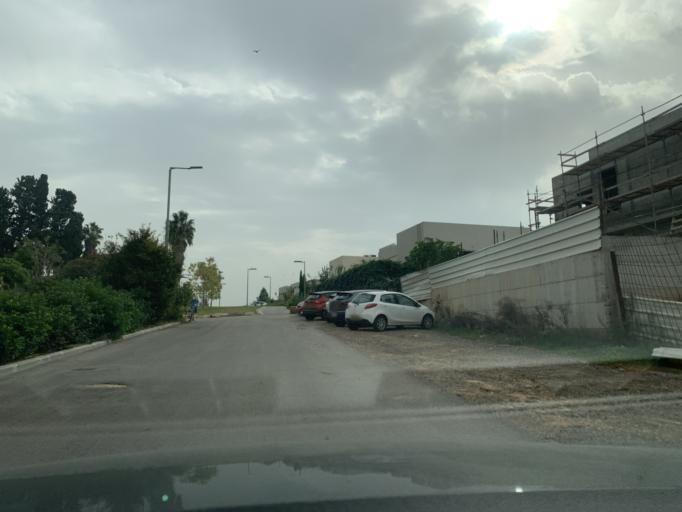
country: IL
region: Central District
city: Tirah
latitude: 32.2172
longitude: 34.9347
